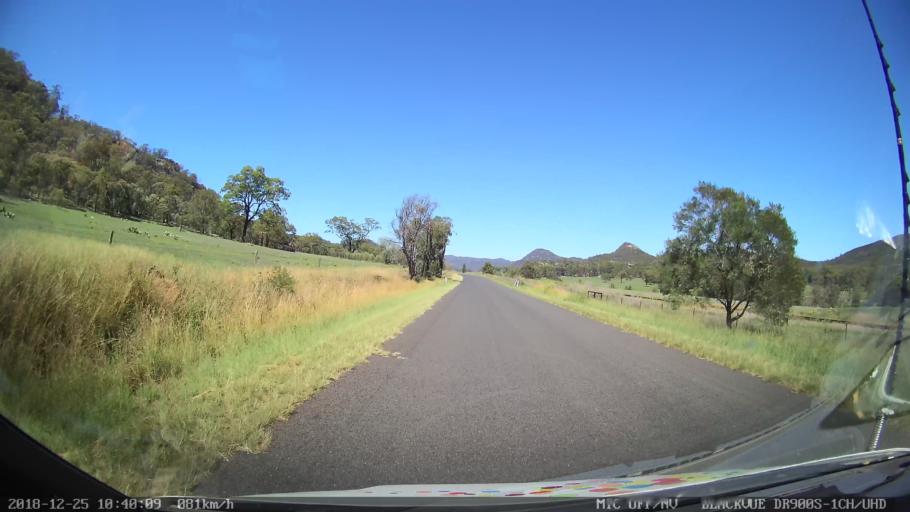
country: AU
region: New South Wales
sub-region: Upper Hunter Shire
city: Merriwa
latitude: -32.4056
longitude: 150.3465
